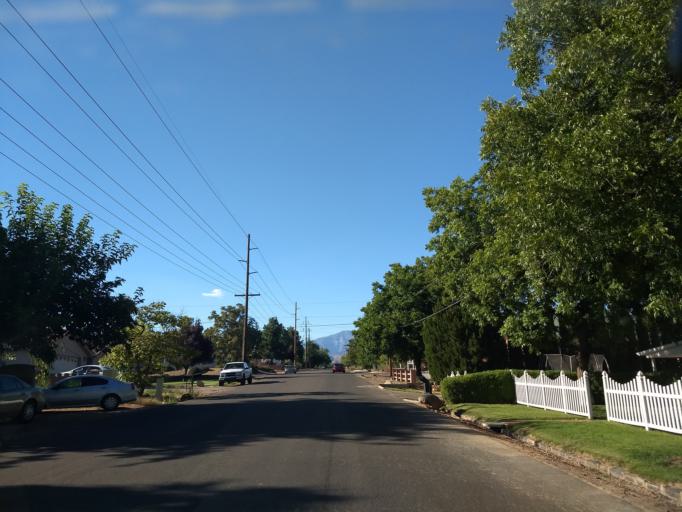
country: US
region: Utah
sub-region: Washington County
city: Washington
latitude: 37.1258
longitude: -113.5082
